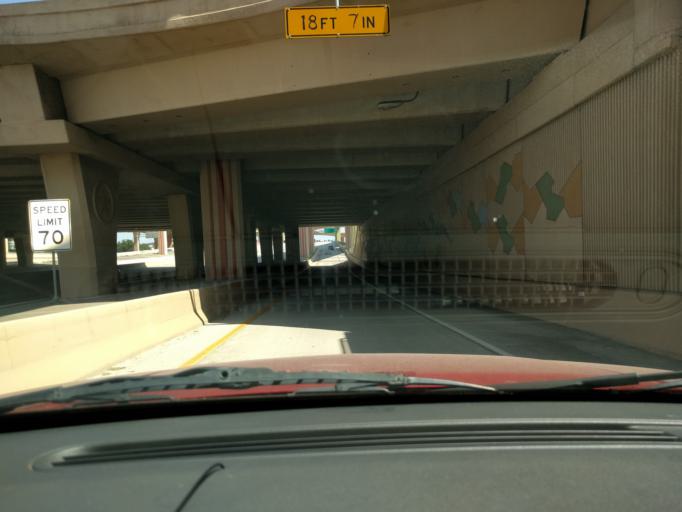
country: US
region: Texas
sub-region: Dallas County
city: Richardson
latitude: 32.9238
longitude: -96.7696
